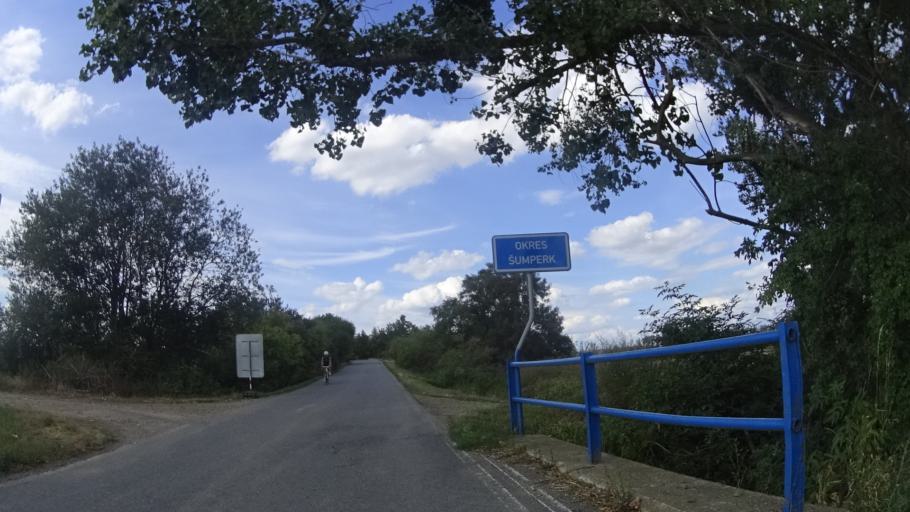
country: CZ
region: Olomoucky
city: Bila Lhota
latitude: 49.7305
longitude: 16.9803
